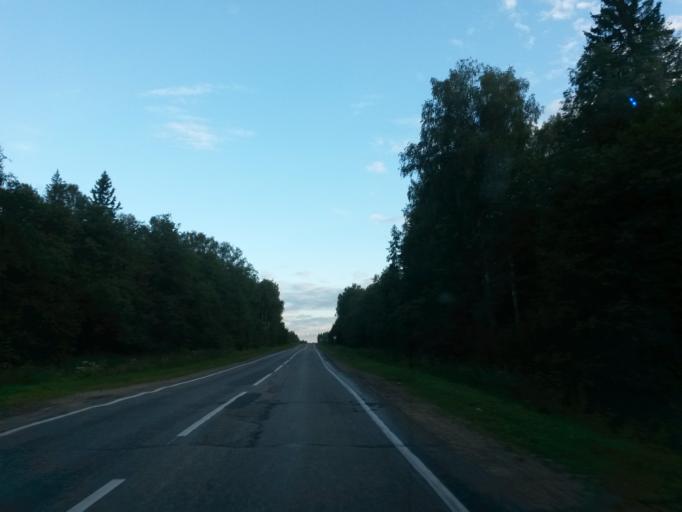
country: RU
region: Jaroslavl
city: Gavrilov-Yam
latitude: 57.4189
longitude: 39.9197
